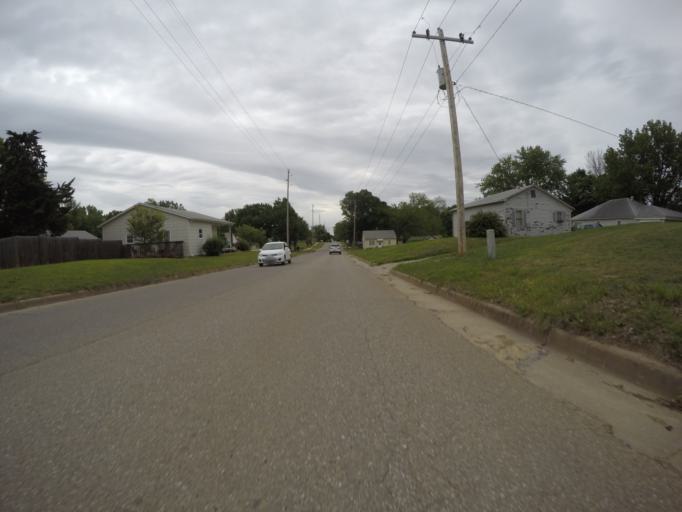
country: US
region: Kansas
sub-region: Pottawatomie County
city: Wamego
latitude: 39.2008
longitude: -96.3139
